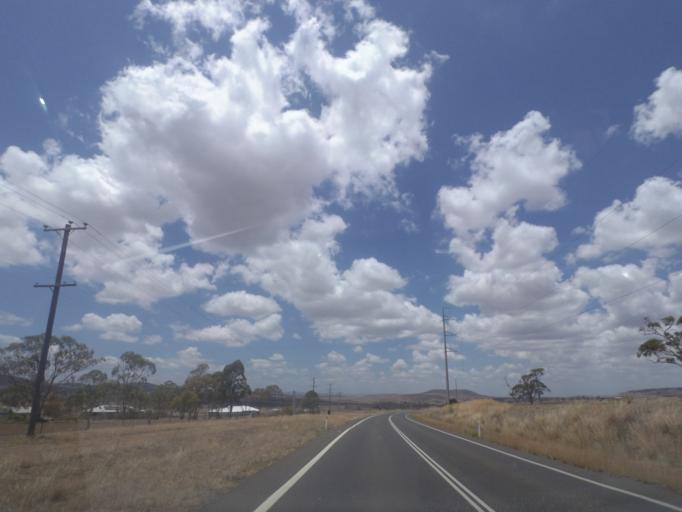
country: AU
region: Queensland
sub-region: Toowoomba
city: Top Camp
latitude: -27.7508
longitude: 151.9333
